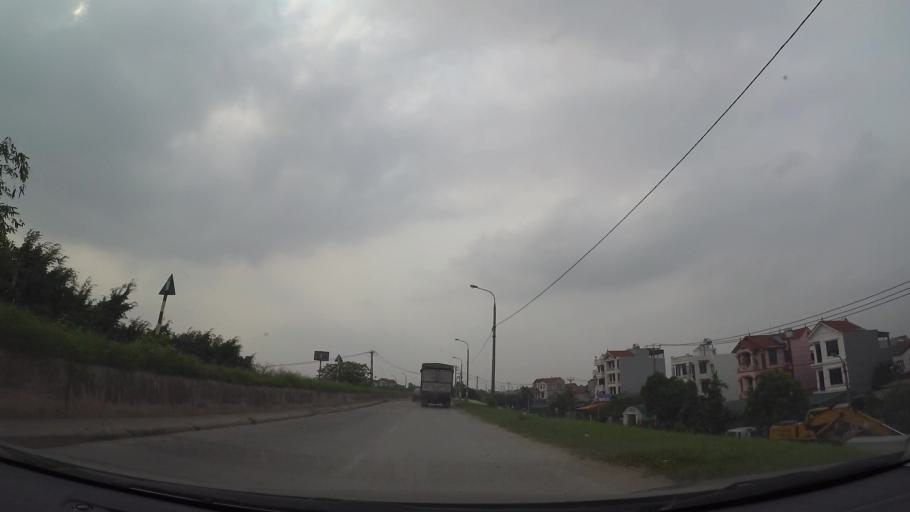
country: VN
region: Ha Noi
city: Trau Quy
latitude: 21.0037
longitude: 105.9088
